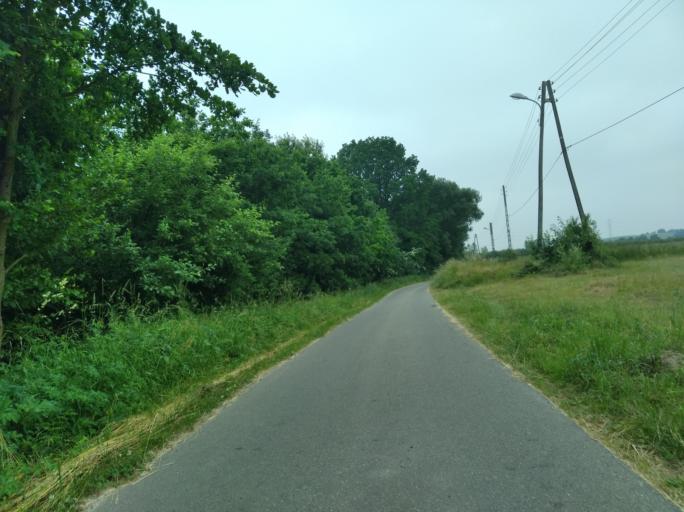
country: PL
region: Subcarpathian Voivodeship
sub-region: Powiat brzozowski
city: Jablonica Polska
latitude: 49.6920
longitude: 21.8885
